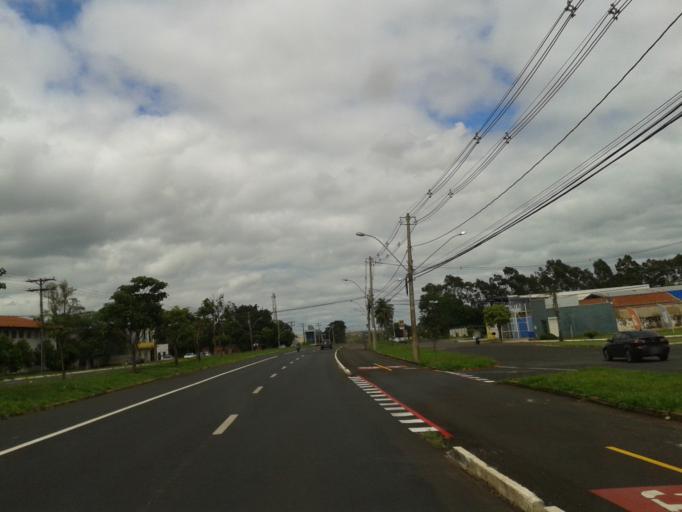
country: BR
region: Minas Gerais
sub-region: Uberaba
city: Uberaba
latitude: -19.7492
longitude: -47.9728
